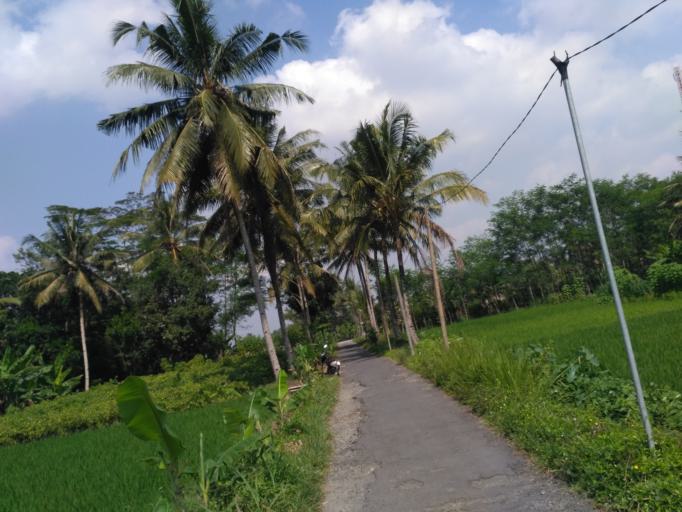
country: ID
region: Daerah Istimewa Yogyakarta
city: Melati
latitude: -7.7067
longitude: 110.4141
